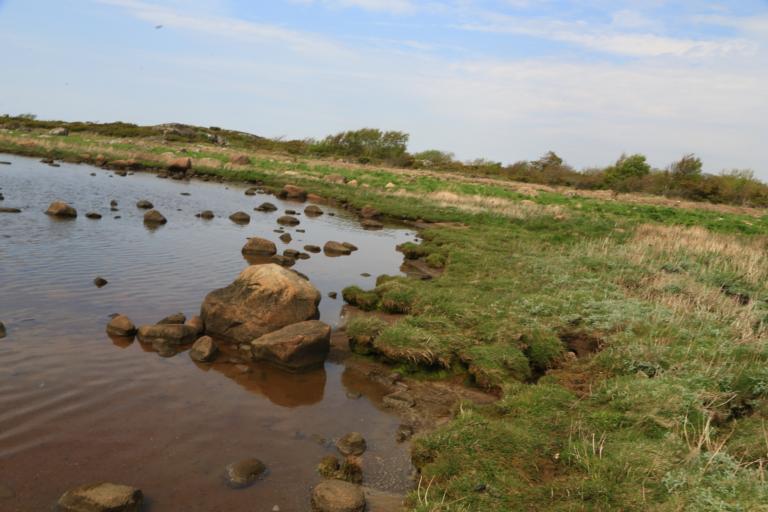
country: SE
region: Halland
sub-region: Varbergs Kommun
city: Varberg
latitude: 57.1473
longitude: 12.2075
